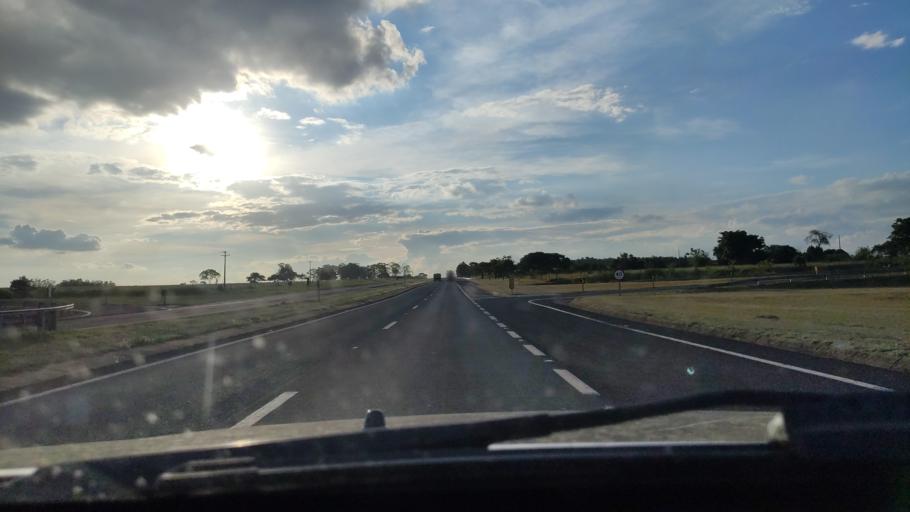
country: BR
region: Sao Paulo
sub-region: Rancharia
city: Rancharia
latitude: -22.4618
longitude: -50.9626
